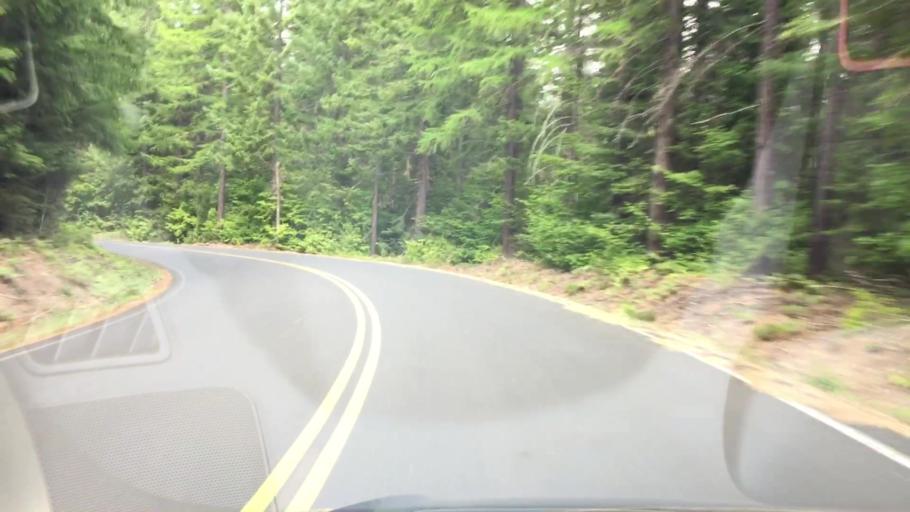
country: US
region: Washington
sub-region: Klickitat County
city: White Salmon
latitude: 46.0877
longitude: -121.6019
